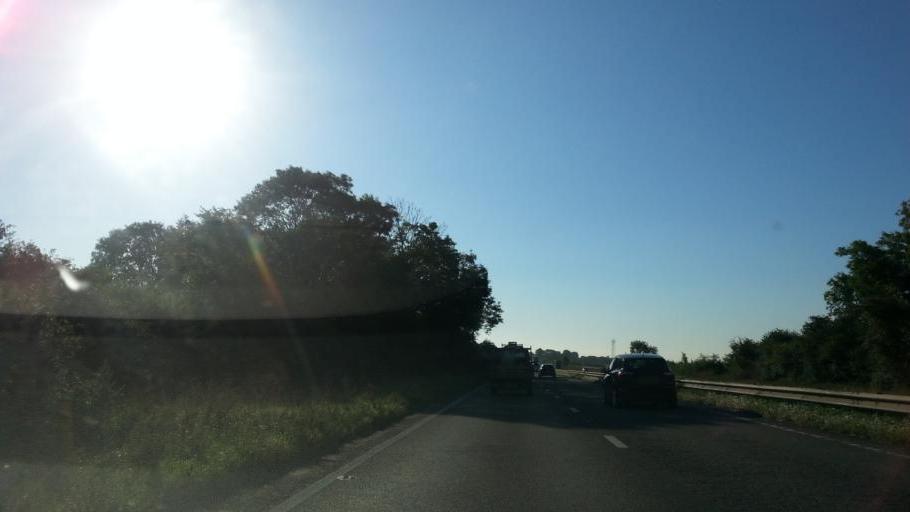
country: GB
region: England
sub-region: Lincolnshire
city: Long Bennington
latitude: 52.9767
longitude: -0.7366
